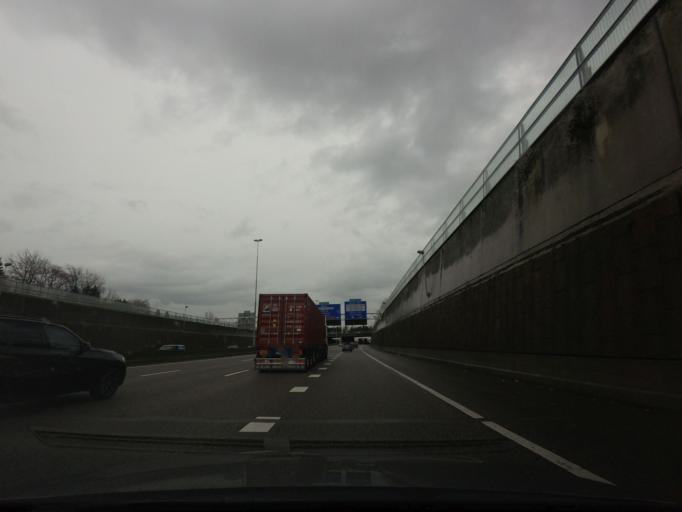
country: NL
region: North Brabant
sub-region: Gemeente Breda
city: Breda
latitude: 51.5980
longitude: 4.7229
